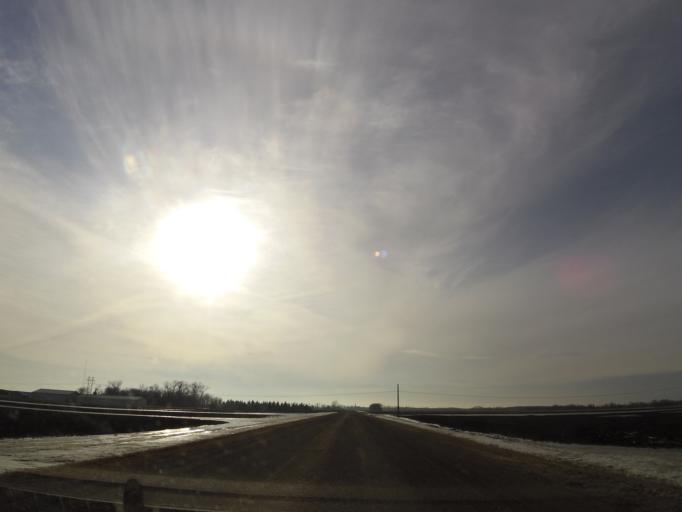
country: US
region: North Dakota
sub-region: Walsh County
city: Grafton
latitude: 48.4266
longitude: -97.2623
